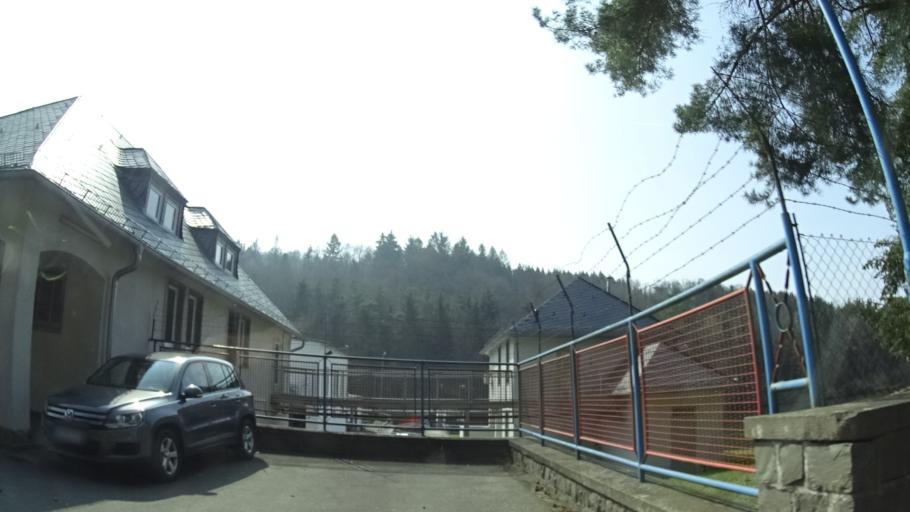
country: DE
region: Rheinland-Pfalz
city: Hoppstadten-Weiersbach
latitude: 49.6148
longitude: 7.2118
